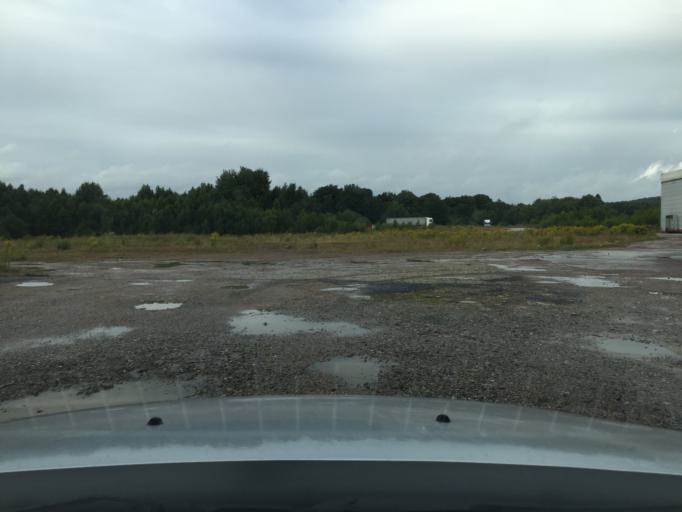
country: SE
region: Skane
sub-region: Hoors Kommun
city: Hoeoer
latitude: 55.9565
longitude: 13.5641
